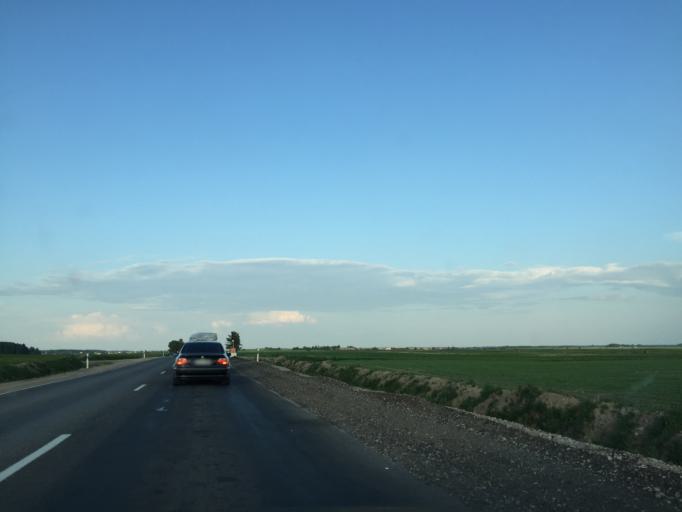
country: LT
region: Telsiu apskritis
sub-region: Telsiai
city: Telsiai
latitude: 56.0045
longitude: 22.3286
